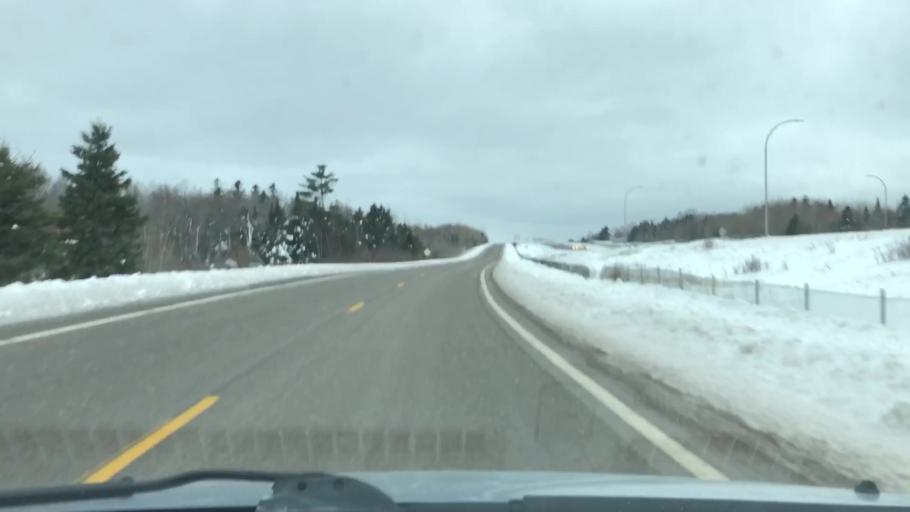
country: US
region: Minnesota
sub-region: Saint Louis County
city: Proctor
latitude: 46.7201
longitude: -92.2400
